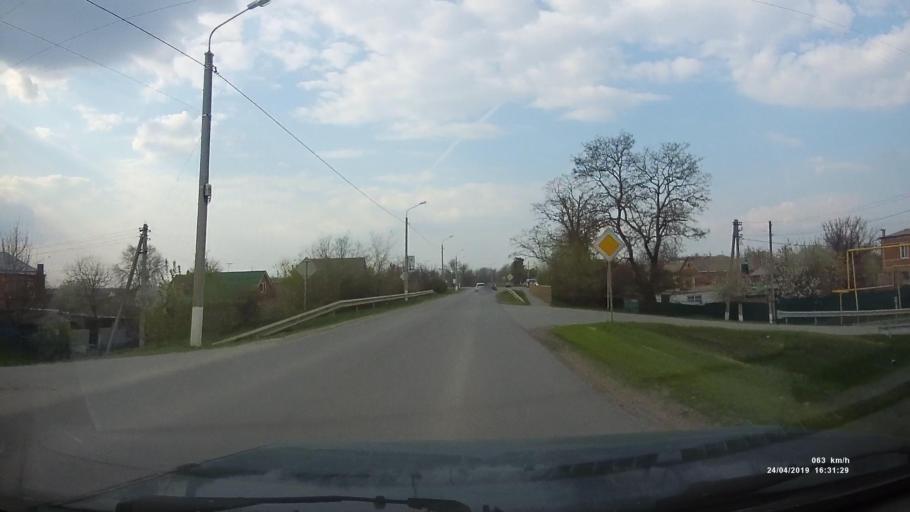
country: RU
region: Rostov
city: Orlovskiy
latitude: 46.8819
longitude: 42.0385
